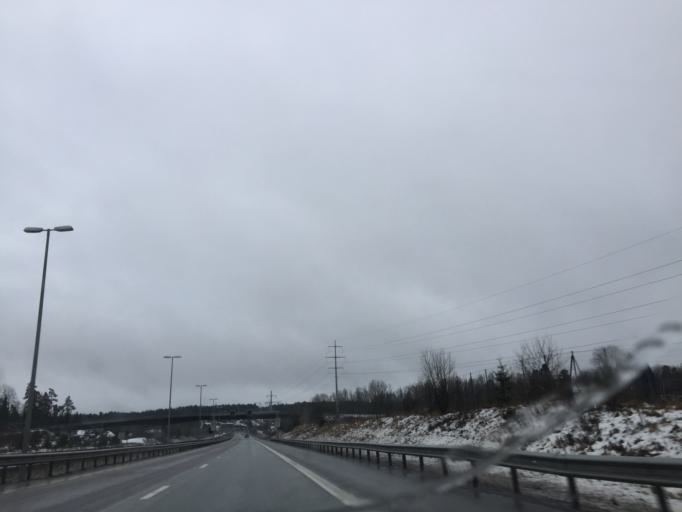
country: NO
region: Akershus
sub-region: Vestby
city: Vestby
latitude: 59.5447
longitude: 10.7242
